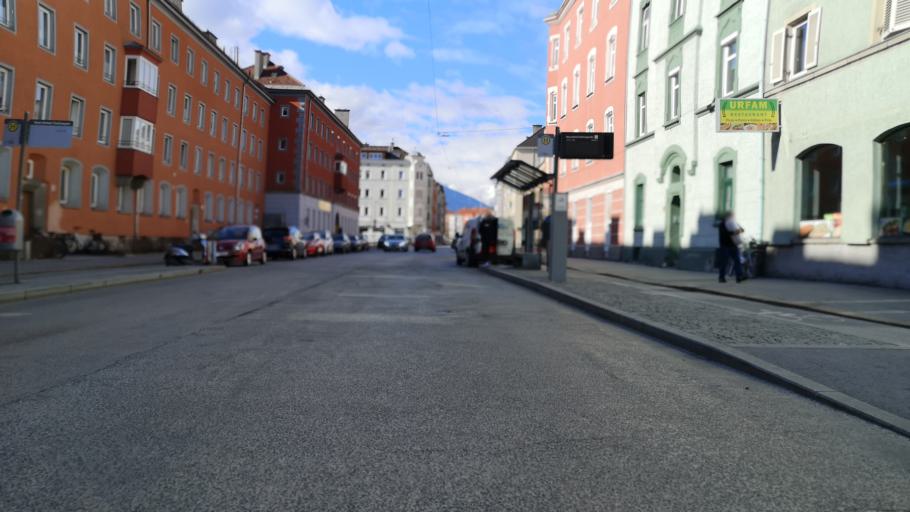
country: AT
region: Tyrol
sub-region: Innsbruck Stadt
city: Innsbruck
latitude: 47.2651
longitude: 11.4131
